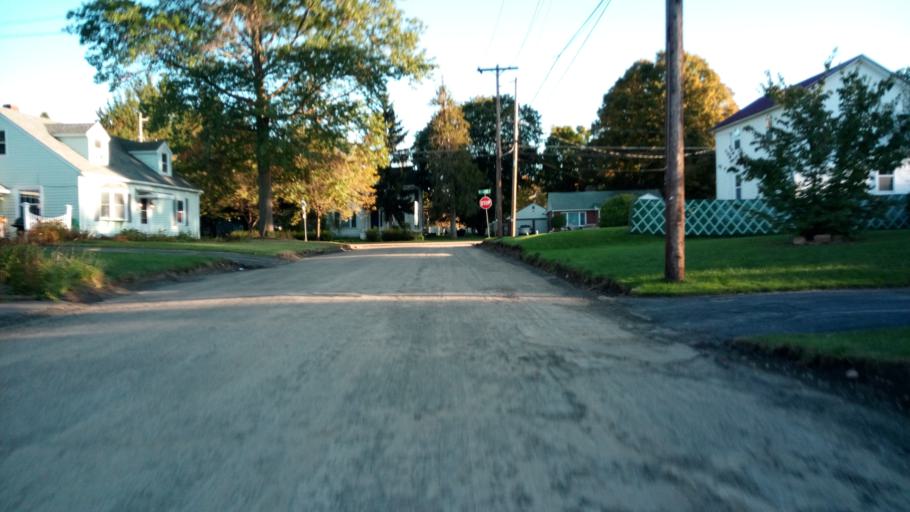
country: US
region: New York
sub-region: Chemung County
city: Elmira
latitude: 42.0768
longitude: -76.8182
